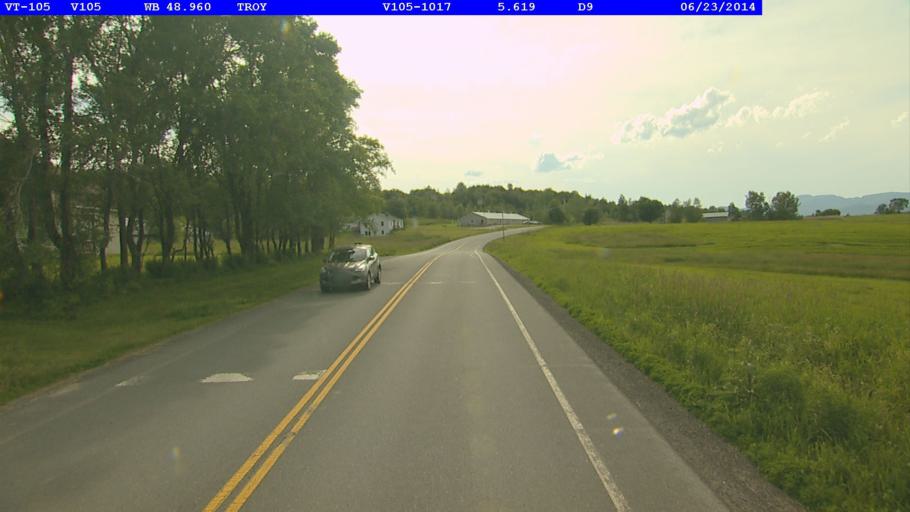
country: US
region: Vermont
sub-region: Orleans County
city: Newport
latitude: 44.9801
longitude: -72.3499
